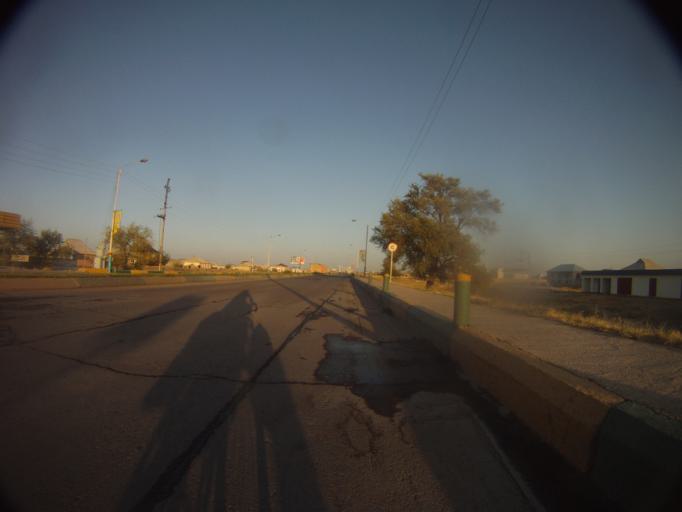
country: KZ
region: Ongtustik Qazaqstan
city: Turkestan
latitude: 43.2826
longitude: 68.3146
